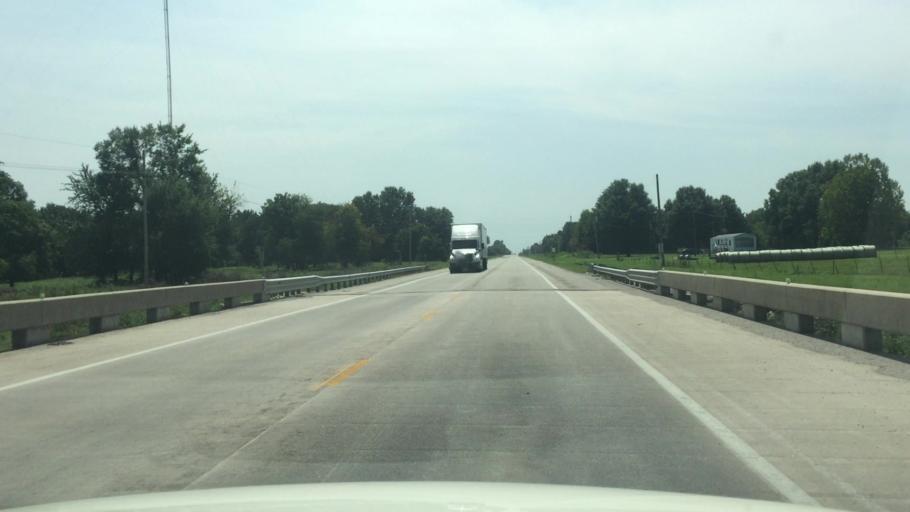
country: US
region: Kansas
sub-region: Cherokee County
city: Galena
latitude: 37.1291
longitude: -94.7044
